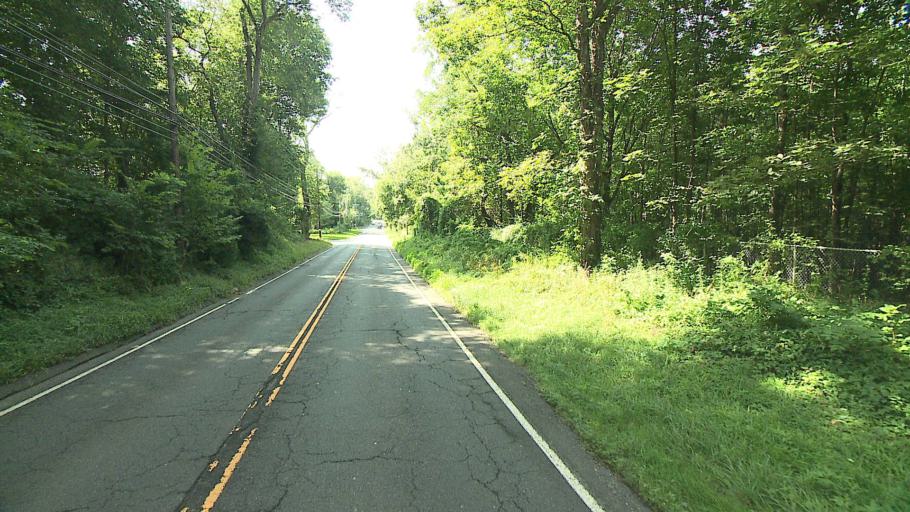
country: US
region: Connecticut
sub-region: Fairfield County
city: Danbury
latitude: 41.4486
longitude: -73.4732
